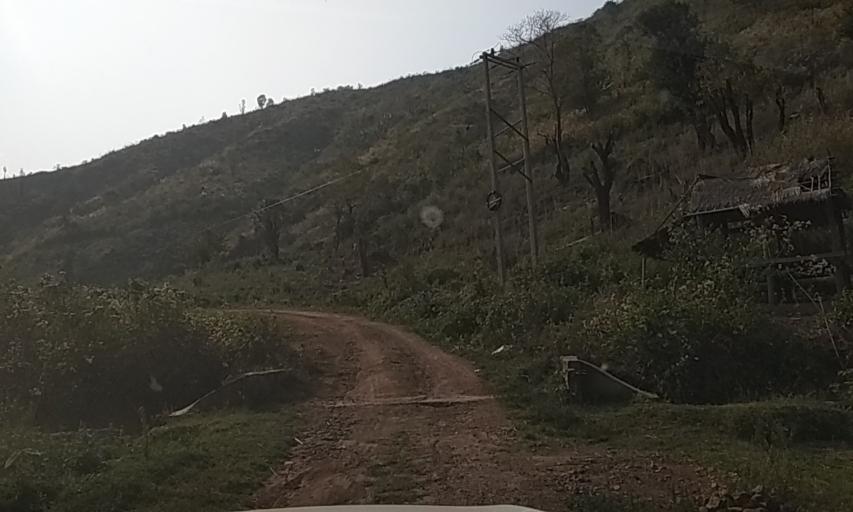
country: LA
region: Louangphabang
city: Louangphabang
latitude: 20.0348
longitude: 101.7937
